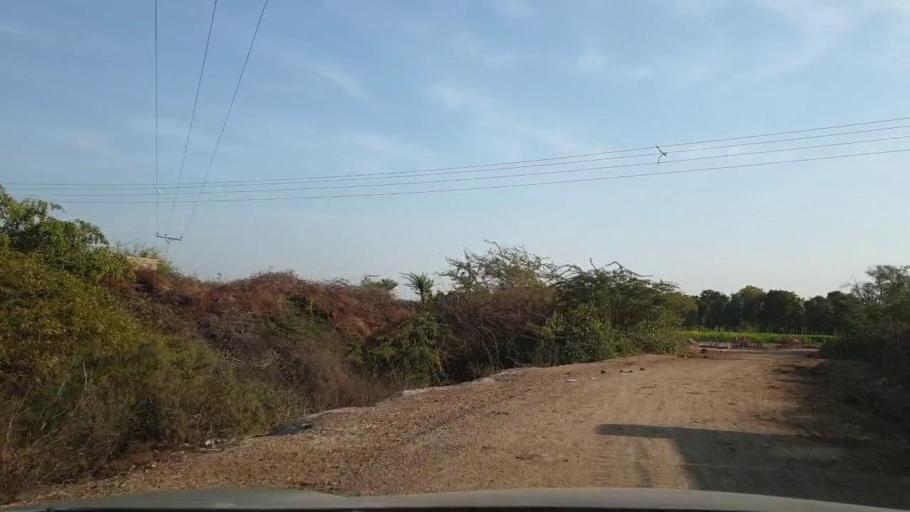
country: PK
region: Sindh
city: Berani
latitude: 25.7299
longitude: 68.7995
